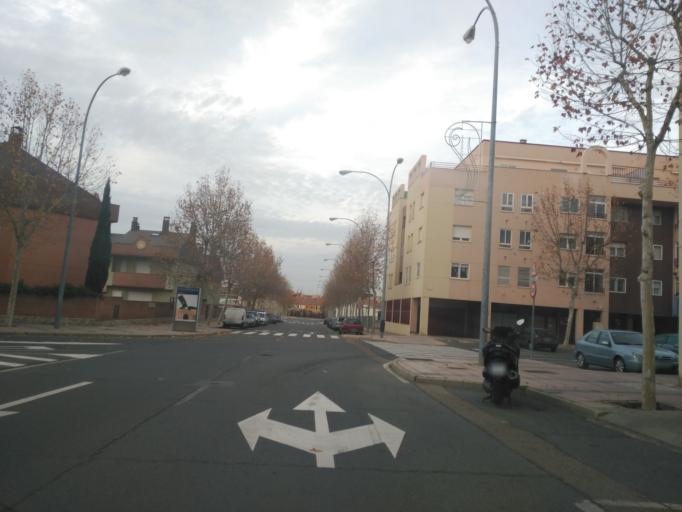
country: ES
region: Castille and Leon
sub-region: Provincia de Salamanca
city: Salamanca
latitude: 40.9476
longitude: -5.6722
